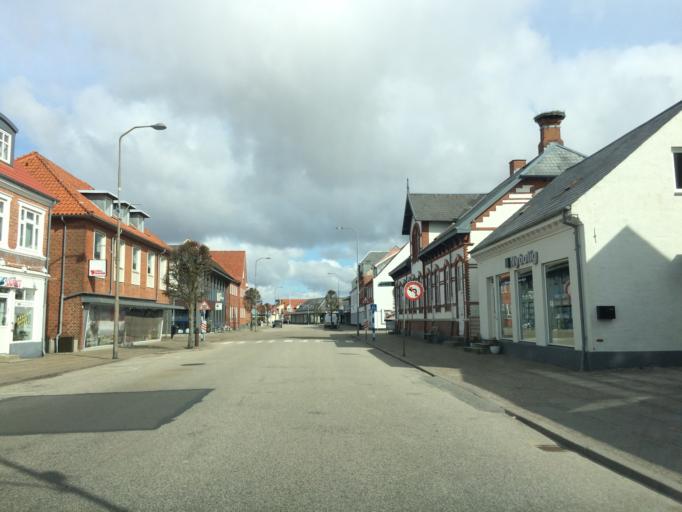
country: DK
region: Central Jutland
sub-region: Ringkobing-Skjern Kommune
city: Tarm
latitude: 55.9071
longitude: 8.5208
